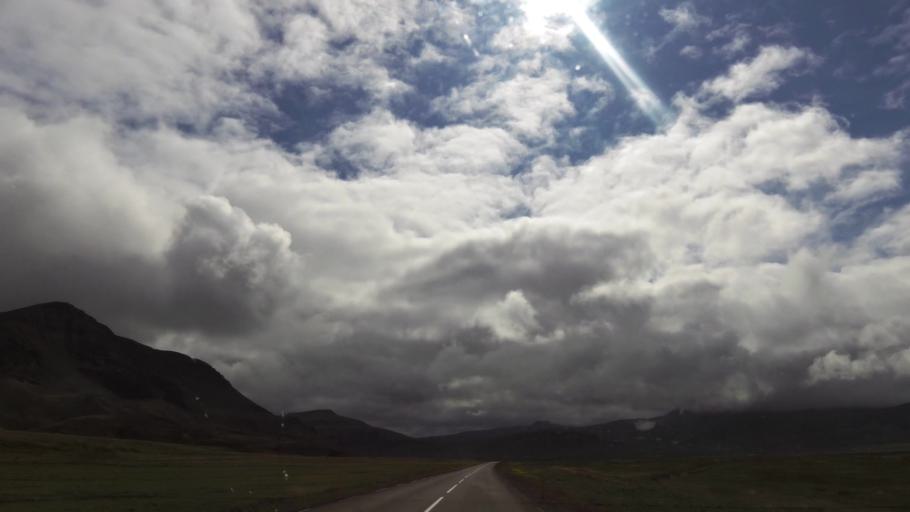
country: IS
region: West
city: Borgarnes
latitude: 65.4026
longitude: -21.8800
